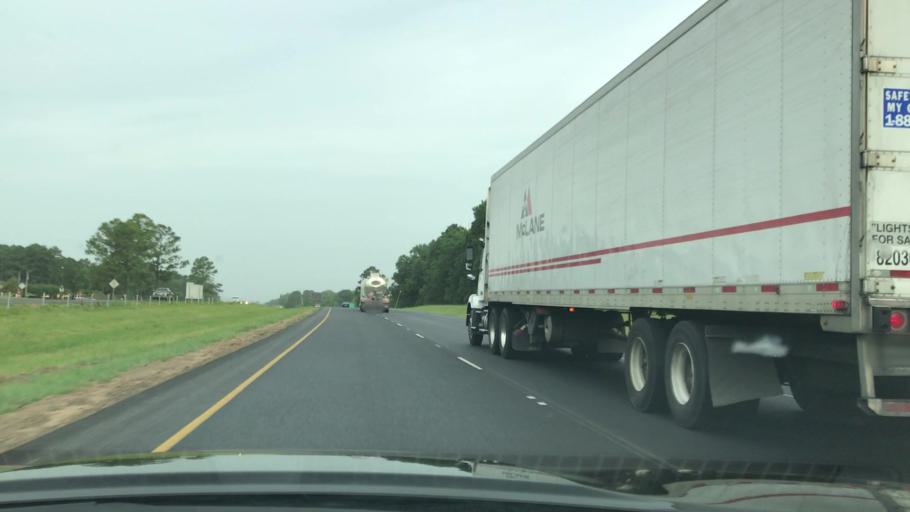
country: US
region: Louisiana
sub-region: Caddo Parish
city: Greenwood
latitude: 32.4515
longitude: -93.9981
